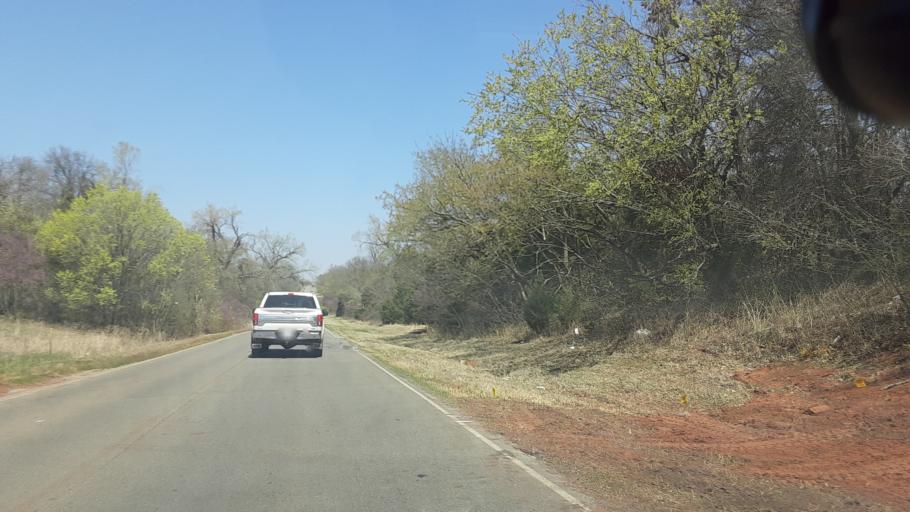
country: US
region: Oklahoma
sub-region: Oklahoma County
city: Edmond
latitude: 35.7364
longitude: -97.4784
